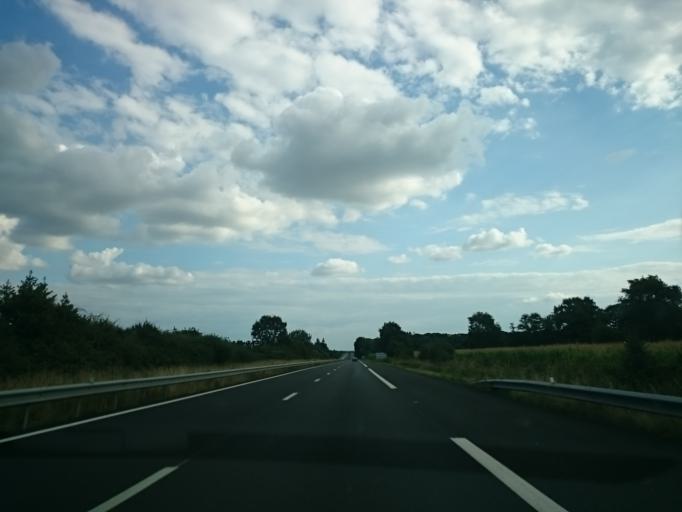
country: FR
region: Pays de la Loire
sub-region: Departement de la Loire-Atlantique
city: La Grigonnais
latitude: 47.5085
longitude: -1.6394
